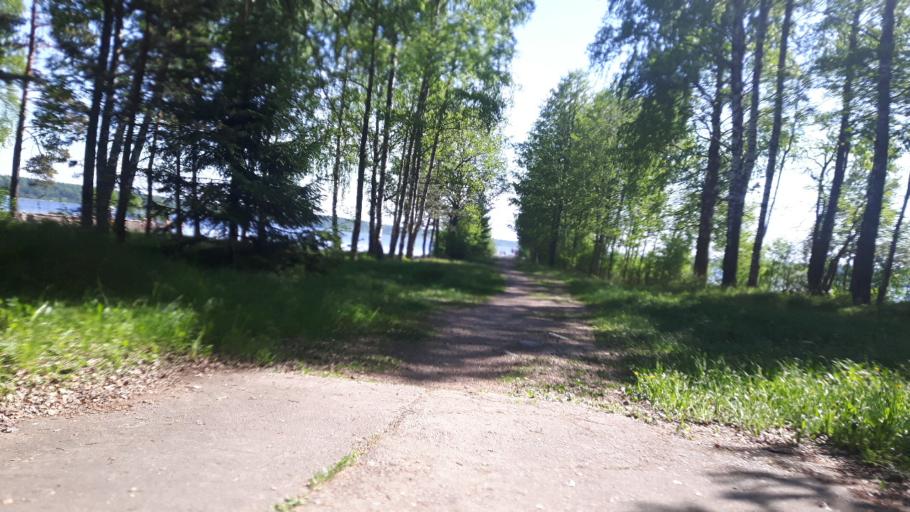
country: RU
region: Leningrad
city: Sista-Palkino
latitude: 59.7620
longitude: 28.7400
